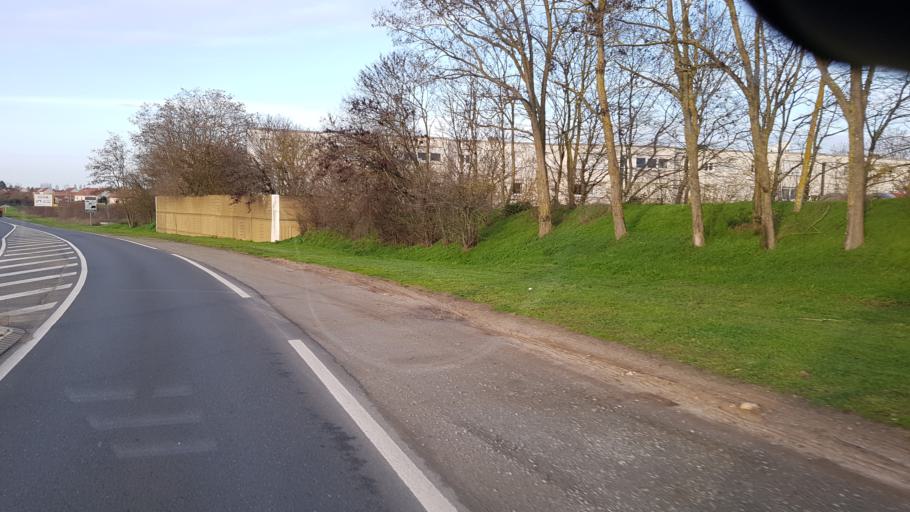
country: FR
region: Centre
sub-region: Departement de l'Indre
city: Chateauroux
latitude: 46.7888
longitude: 1.6902
